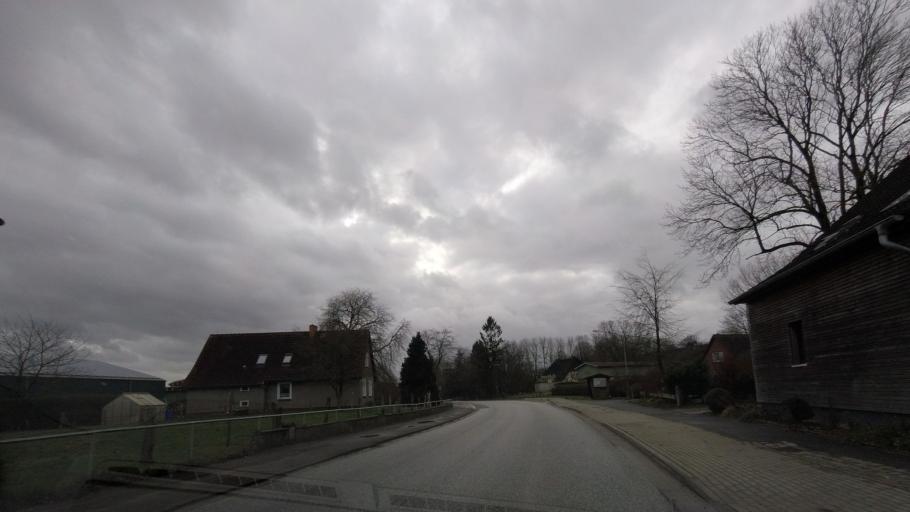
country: DE
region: Schleswig-Holstein
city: Tolk
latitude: 54.5870
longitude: 9.6671
